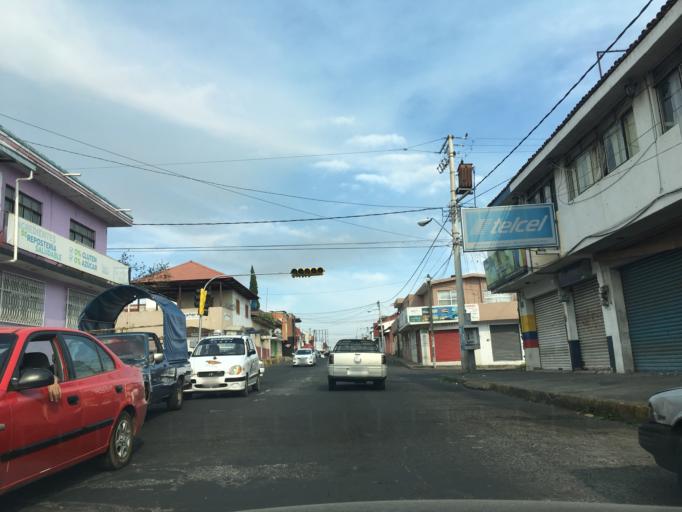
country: MX
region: Michoacan
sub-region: Uruapan
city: Uruapan
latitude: 19.4168
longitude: -102.0587
